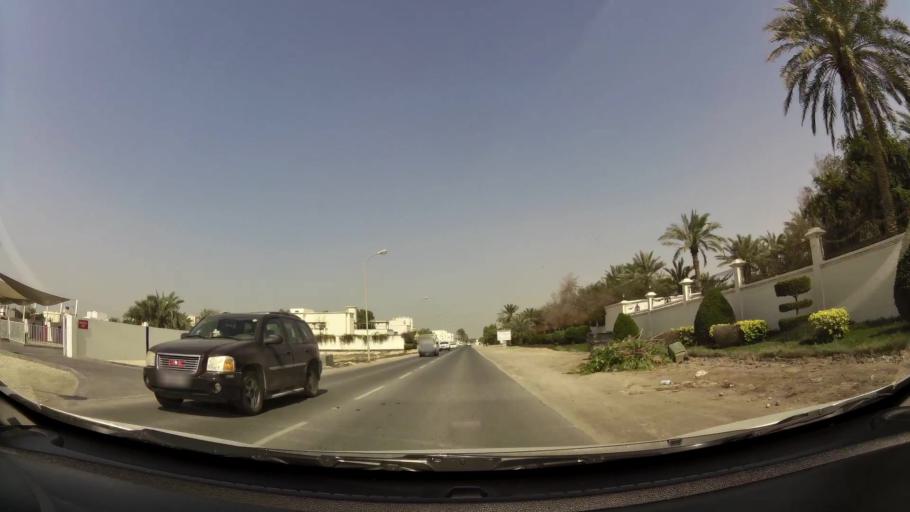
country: BH
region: Northern
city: Madinat `Isa
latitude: 26.1922
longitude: 50.4662
